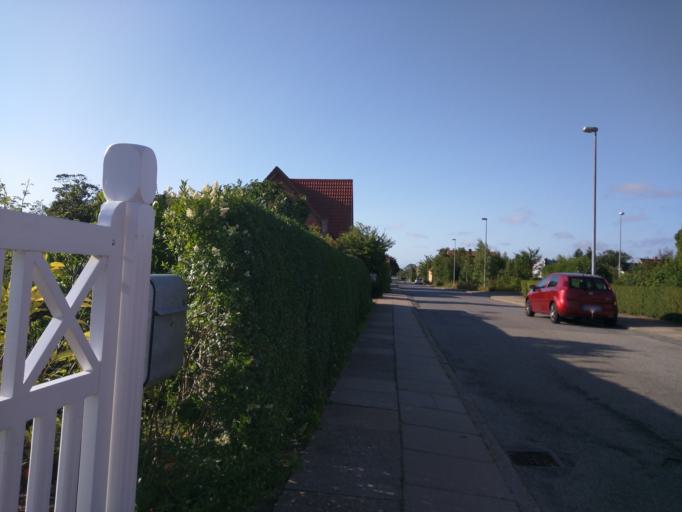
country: DK
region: North Denmark
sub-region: Frederikshavn Kommune
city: Saeby
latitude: 57.3327
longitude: 10.5180
